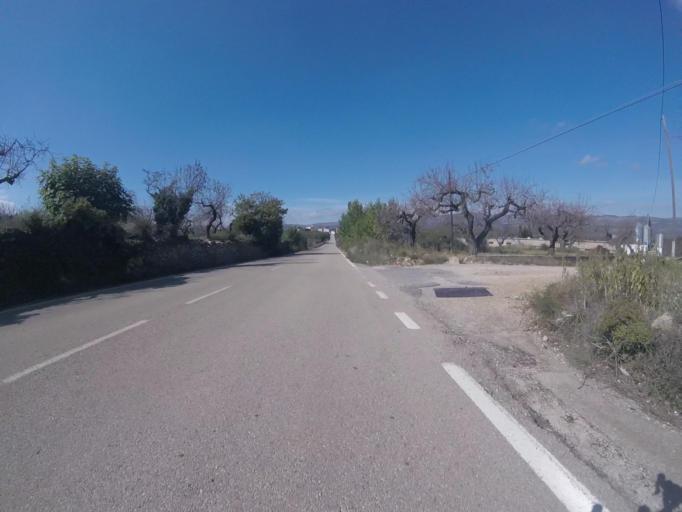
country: ES
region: Valencia
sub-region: Provincia de Castello
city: Albocasser
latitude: 40.3575
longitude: 0.0356
